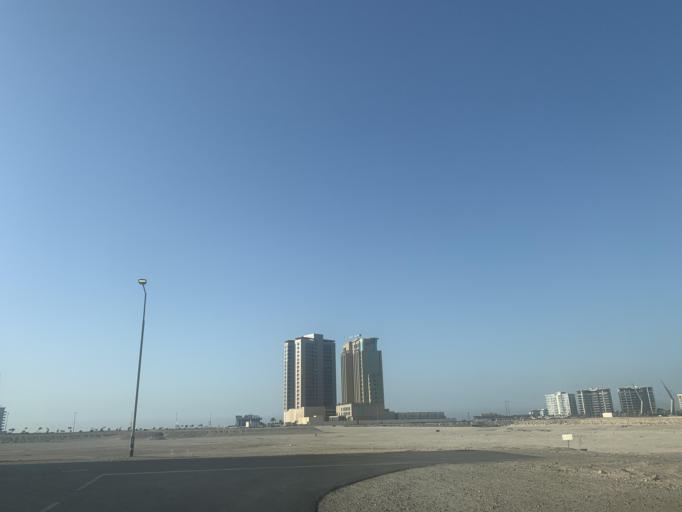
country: BH
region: Manama
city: Jidd Hafs
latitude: 26.2376
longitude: 50.5563
